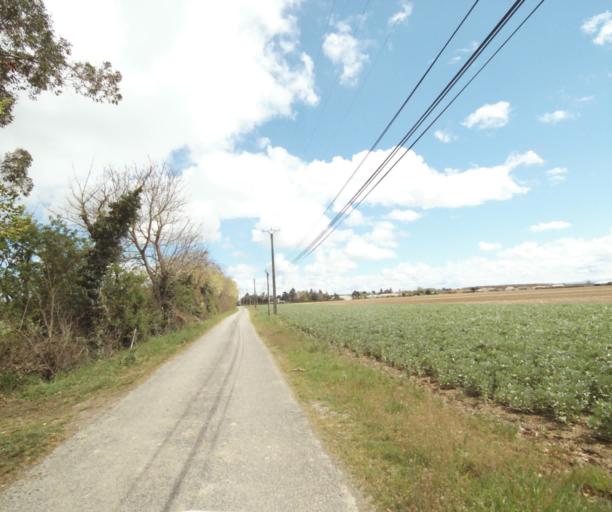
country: FR
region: Midi-Pyrenees
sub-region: Departement de l'Ariege
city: Saverdun
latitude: 43.2451
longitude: 1.6050
